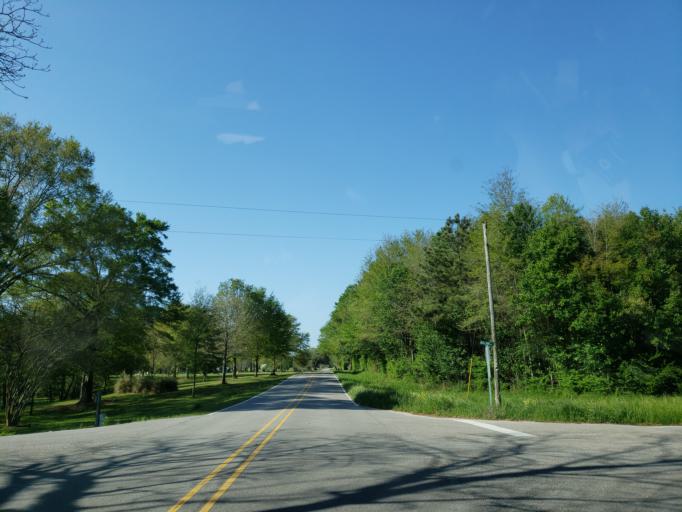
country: US
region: Mississippi
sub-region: Jones County
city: Ellisville
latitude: 31.5869
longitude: -89.3788
